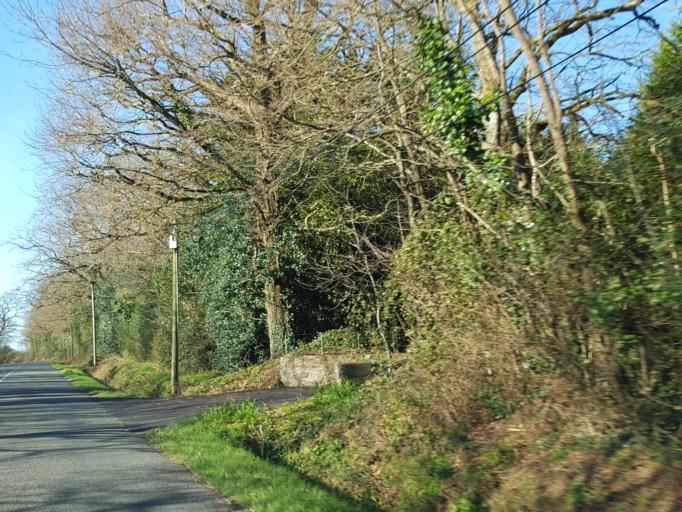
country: FR
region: Pays de la Loire
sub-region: Departement de la Vendee
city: Venansault
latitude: 46.6825
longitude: -1.4997
